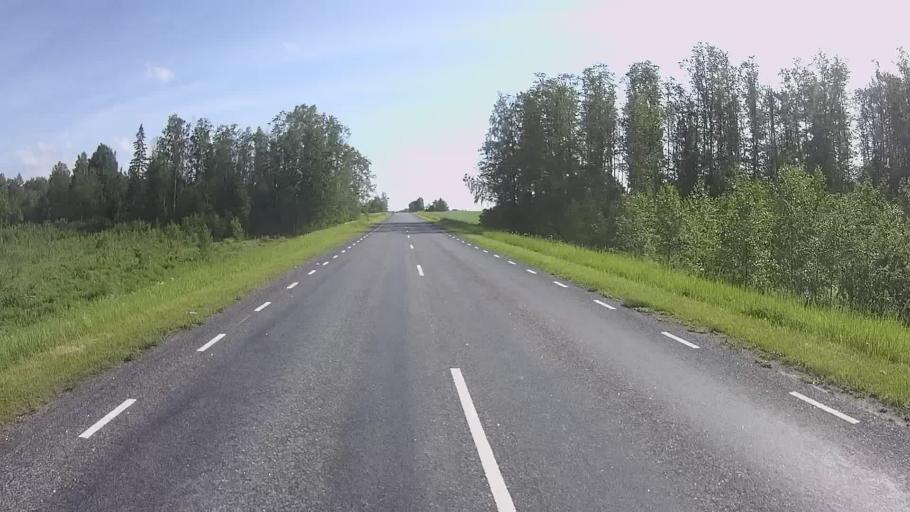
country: EE
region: Valgamaa
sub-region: Torva linn
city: Torva
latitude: 58.0627
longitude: 26.0222
